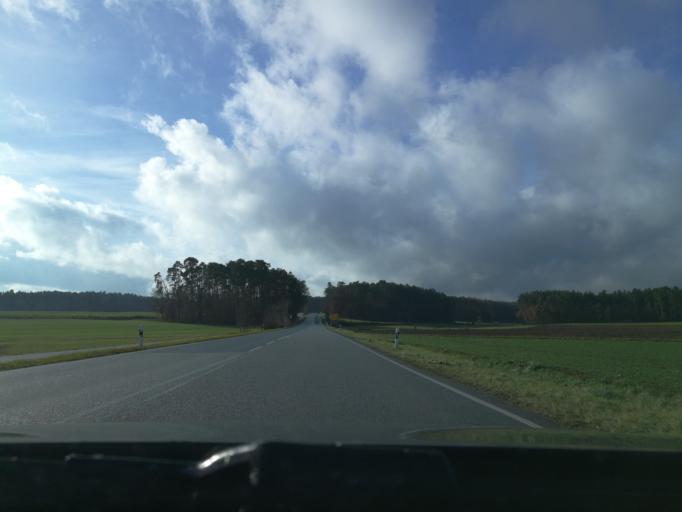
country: DE
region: Bavaria
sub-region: Regierungsbezirk Mittelfranken
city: Kammerstein
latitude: 49.2924
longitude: 10.9611
